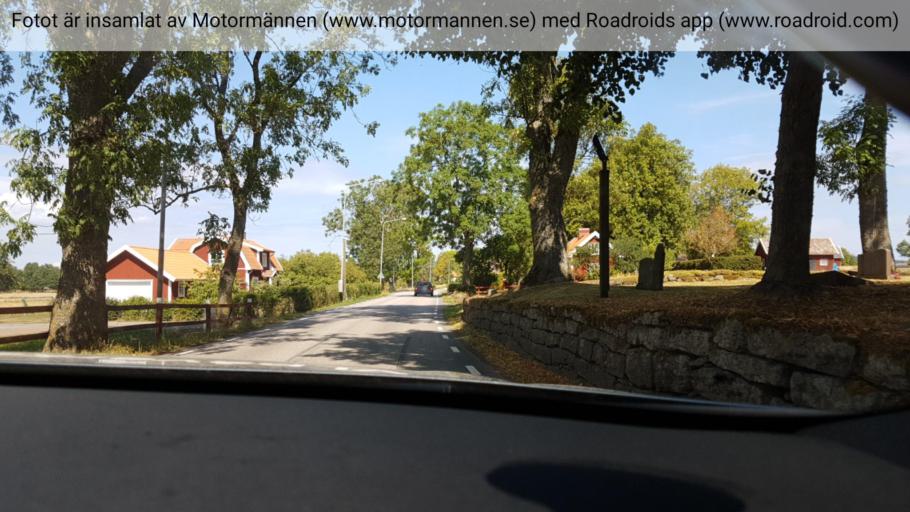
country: SE
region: Vaestra Goetaland
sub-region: Gotene Kommun
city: Kallby
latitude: 58.5602
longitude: 13.3501
